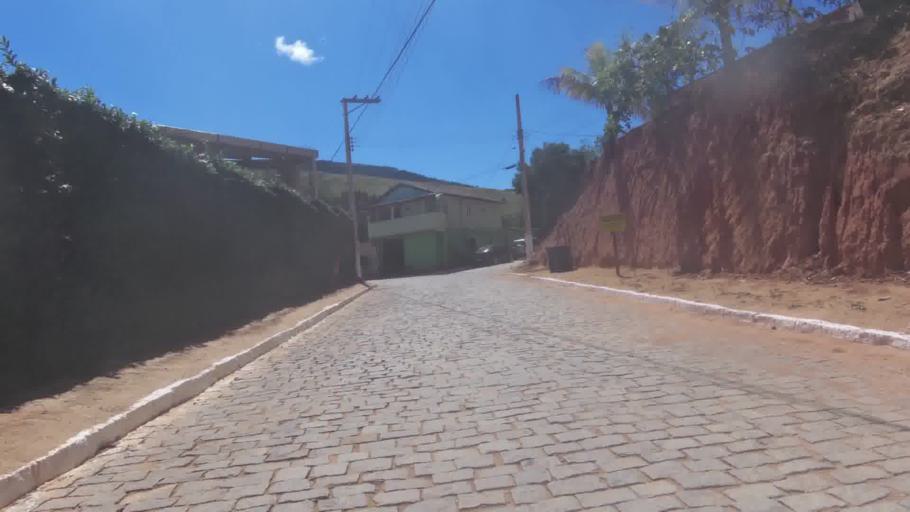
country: BR
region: Espirito Santo
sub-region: Cachoeiro De Itapemirim
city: Cachoeiro de Itapemirim
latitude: -20.9203
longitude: -41.1806
